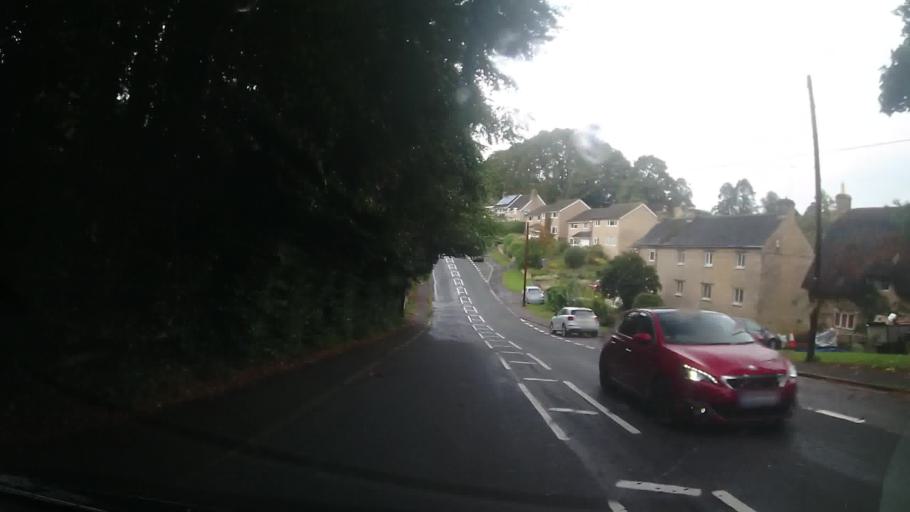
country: GB
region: England
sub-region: Oxfordshire
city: Charlbury
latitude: 51.8715
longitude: -1.4760
